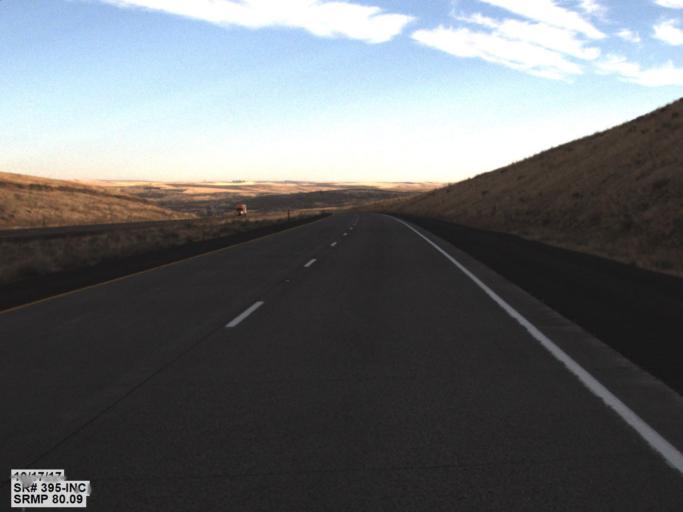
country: US
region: Washington
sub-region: Adams County
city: Ritzville
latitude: 46.9414
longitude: -118.5819
